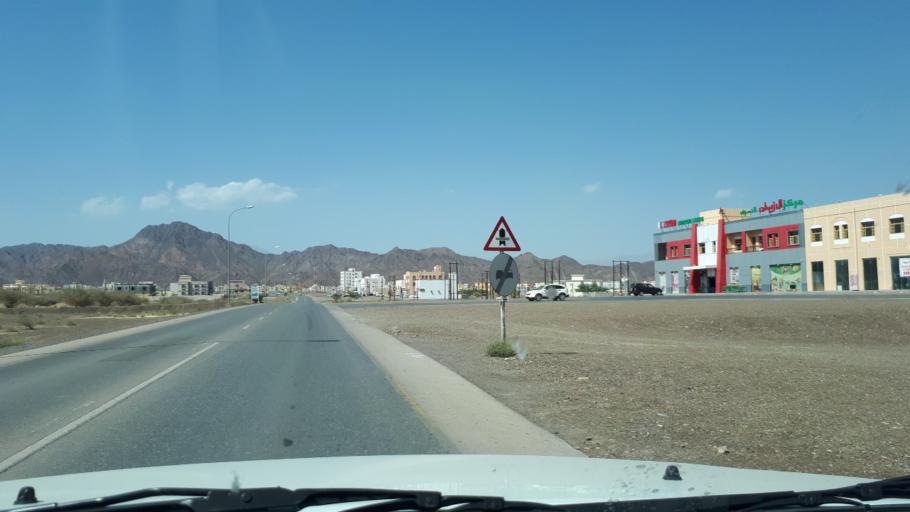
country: OM
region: Muhafazat ad Dakhiliyah
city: Bahla'
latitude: 22.9387
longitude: 57.2587
